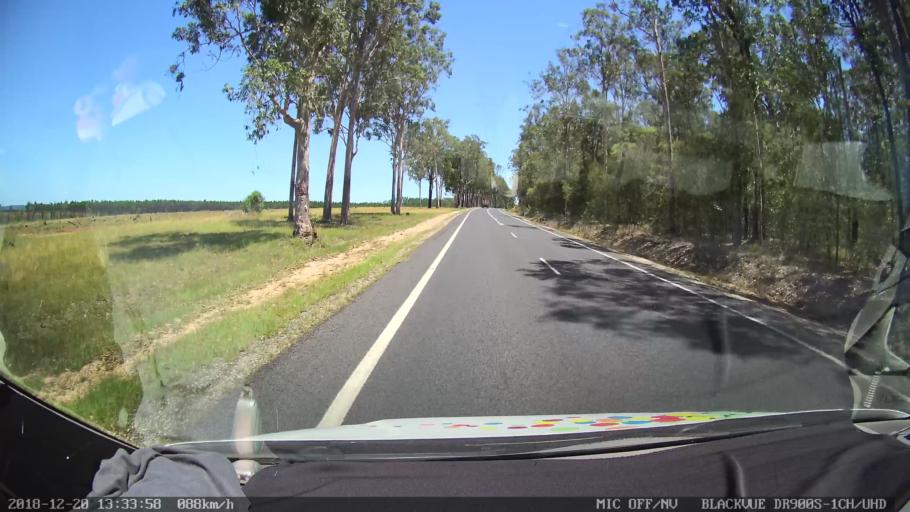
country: AU
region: New South Wales
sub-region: Clarence Valley
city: Gordon
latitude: -29.2526
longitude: 152.9849
